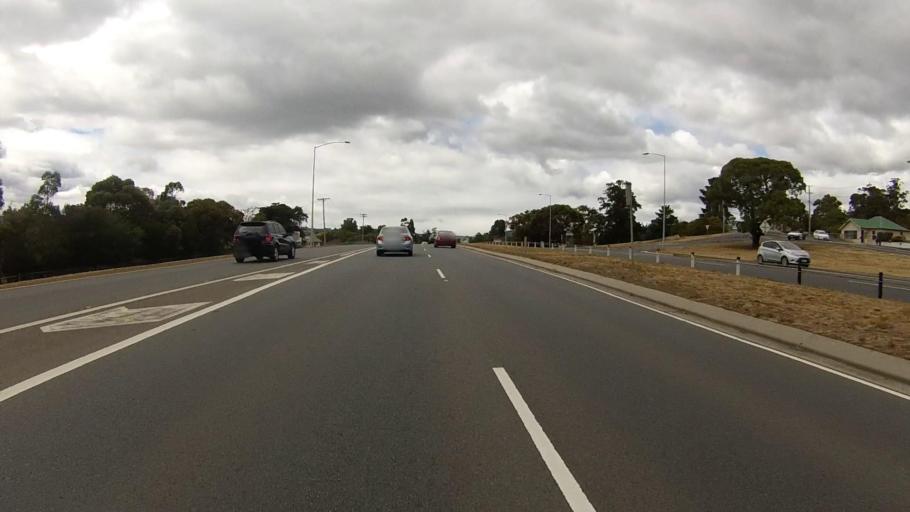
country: AU
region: Tasmania
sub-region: Glenorchy
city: Berriedale
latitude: -42.8177
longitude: 147.2600
